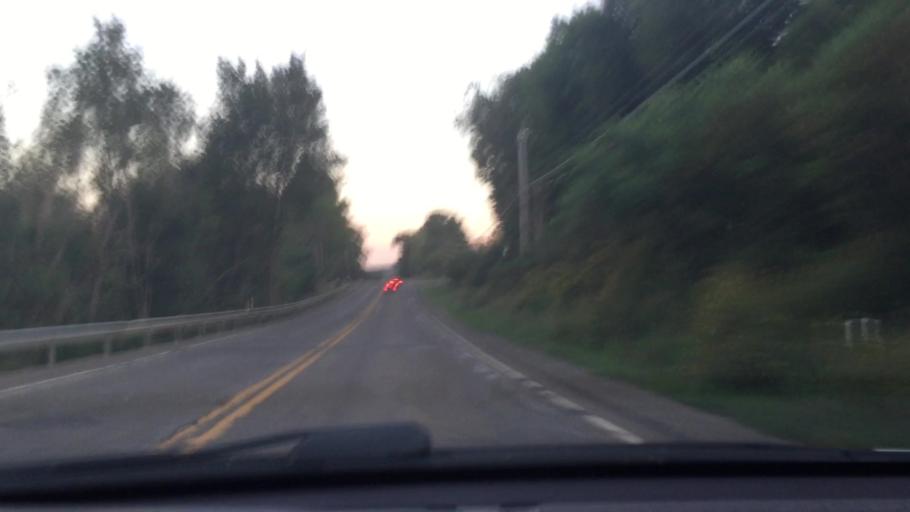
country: US
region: Pennsylvania
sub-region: Butler County
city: Slippery Rock
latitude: 41.1100
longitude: -80.0546
